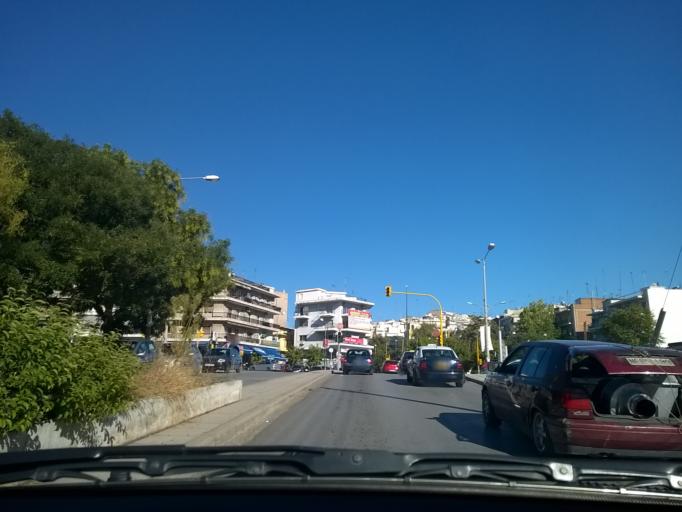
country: GR
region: Central Macedonia
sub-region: Nomos Thessalonikis
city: Thessaloniki
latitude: 40.6483
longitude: 22.9347
